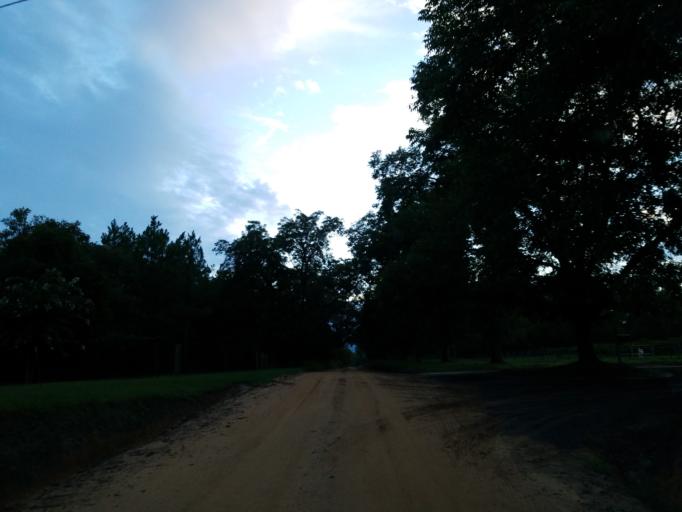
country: US
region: Georgia
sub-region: Tift County
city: Tifton
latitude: 31.5310
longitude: -83.5088
